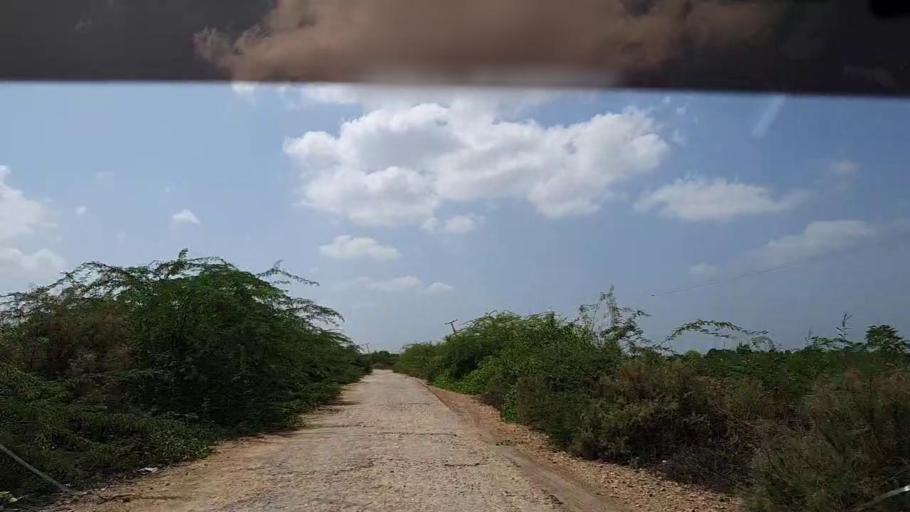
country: PK
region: Sindh
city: Badin
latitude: 24.5758
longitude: 68.7735
